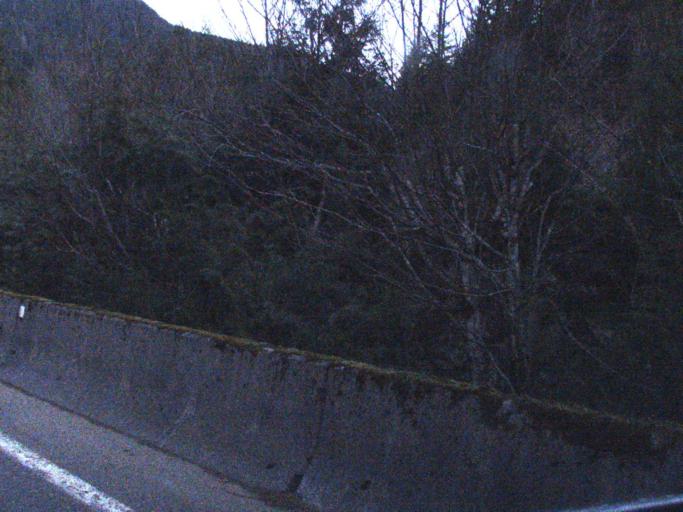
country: US
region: Washington
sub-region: Snohomish County
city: Darrington
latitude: 48.6102
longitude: -121.3619
